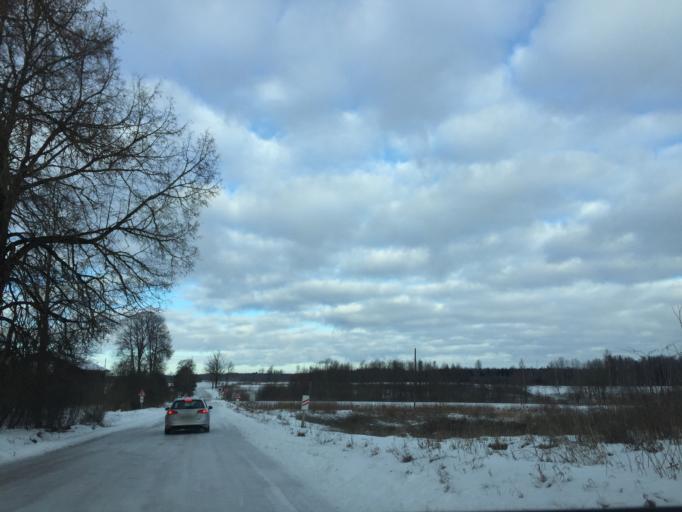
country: LV
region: Lielvarde
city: Lielvarde
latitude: 56.5798
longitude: 24.7355
